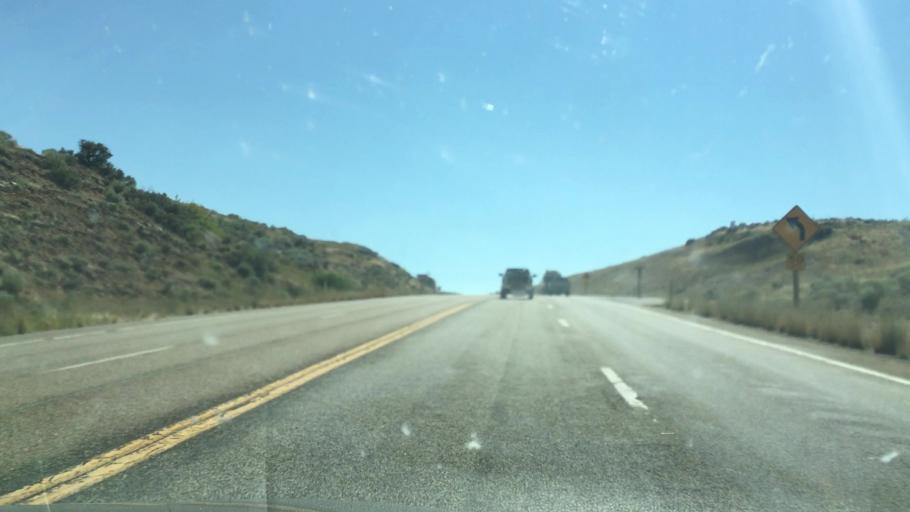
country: US
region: Idaho
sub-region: Ada County
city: Eagle
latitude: 43.8386
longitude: -116.2415
